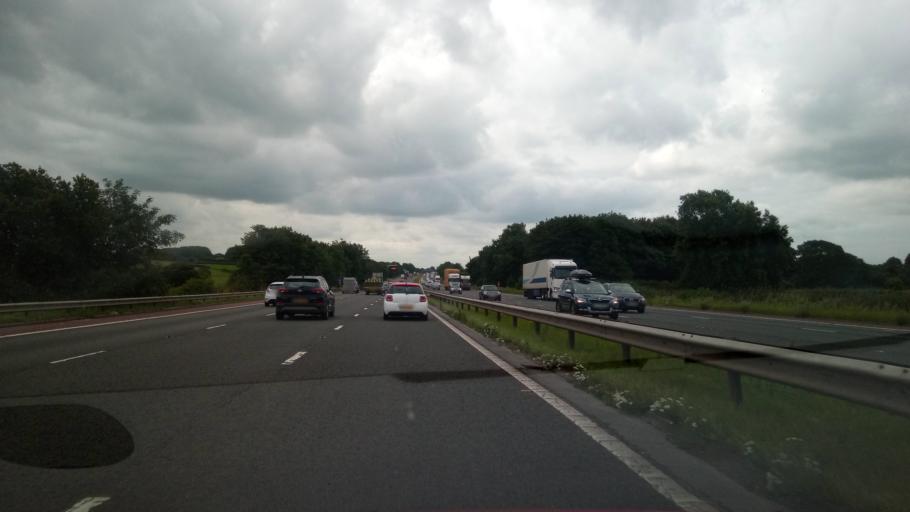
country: GB
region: England
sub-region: Lancashire
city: Galgate
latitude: 54.0038
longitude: -2.7804
